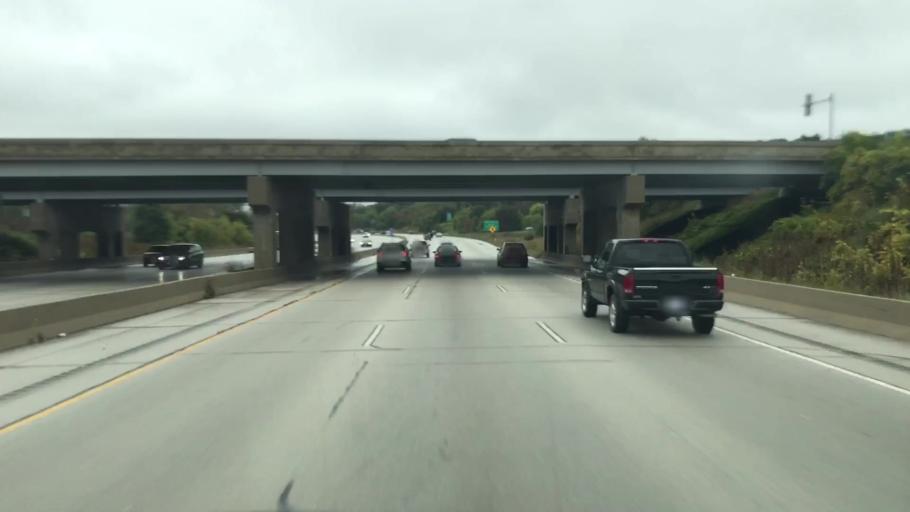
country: US
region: Wisconsin
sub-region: Waukesha County
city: Waukesha
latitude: 43.0479
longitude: -88.2072
